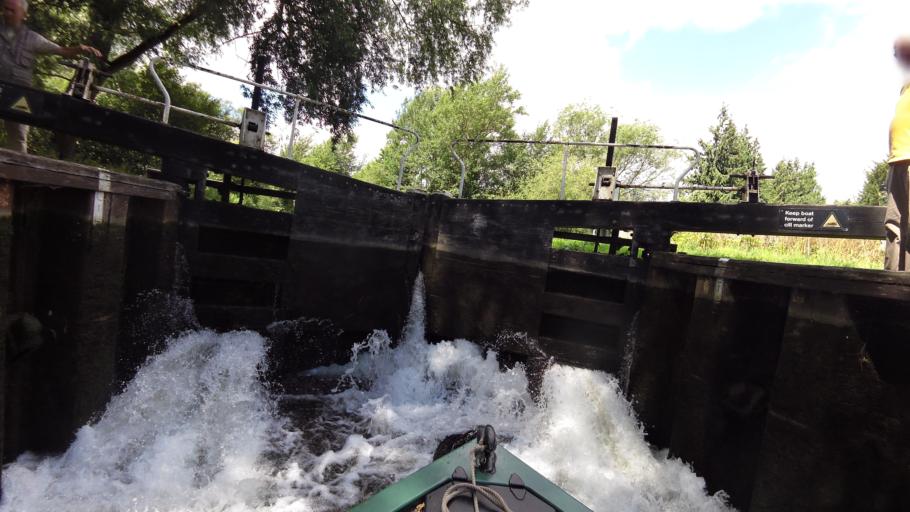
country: GB
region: England
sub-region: West Berkshire
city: Greenham
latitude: 51.4022
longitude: -1.3012
